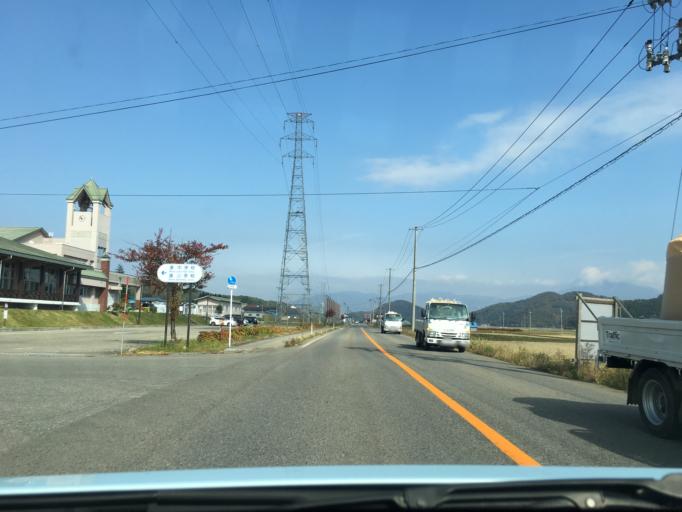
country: JP
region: Fukushima
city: Inawashiro
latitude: 37.4686
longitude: 140.0123
